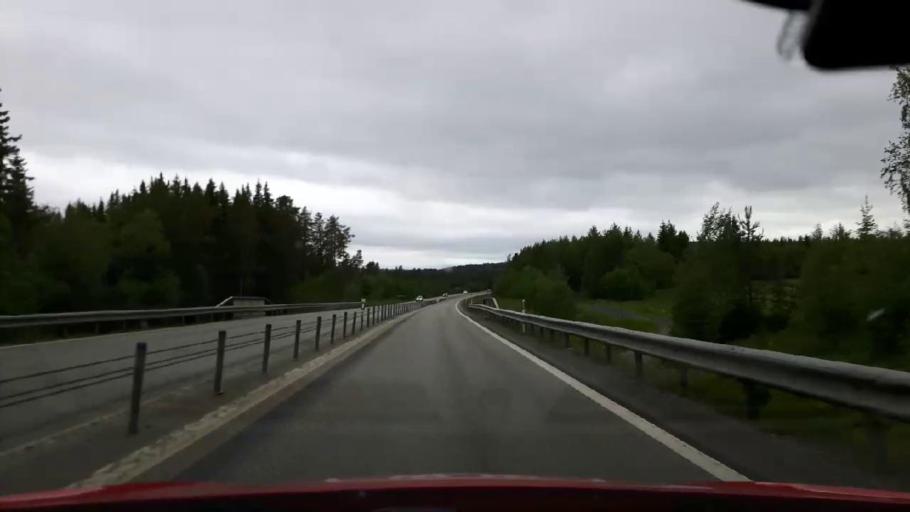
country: SE
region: Jaemtland
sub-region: OEstersunds Kommun
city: Ostersund
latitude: 63.1702
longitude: 14.7069
